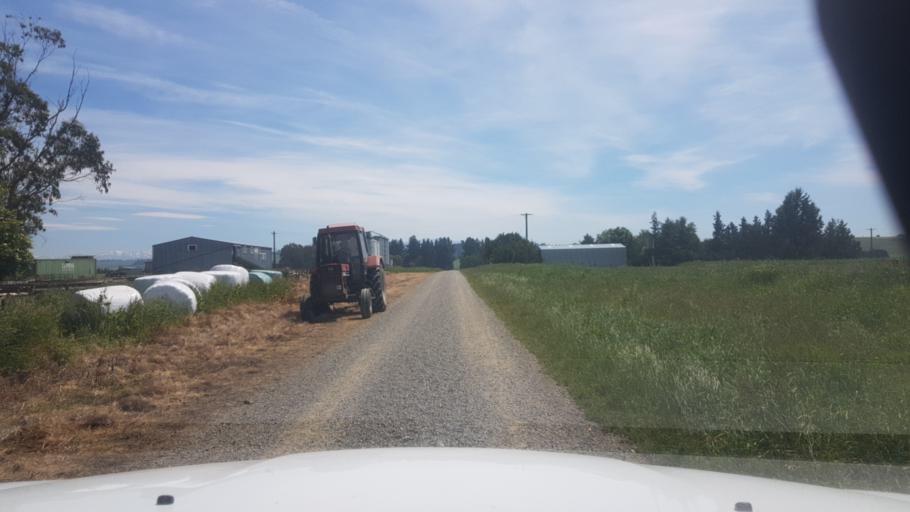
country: NZ
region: Canterbury
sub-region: Timaru District
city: Pleasant Point
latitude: -44.2258
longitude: 171.1646
